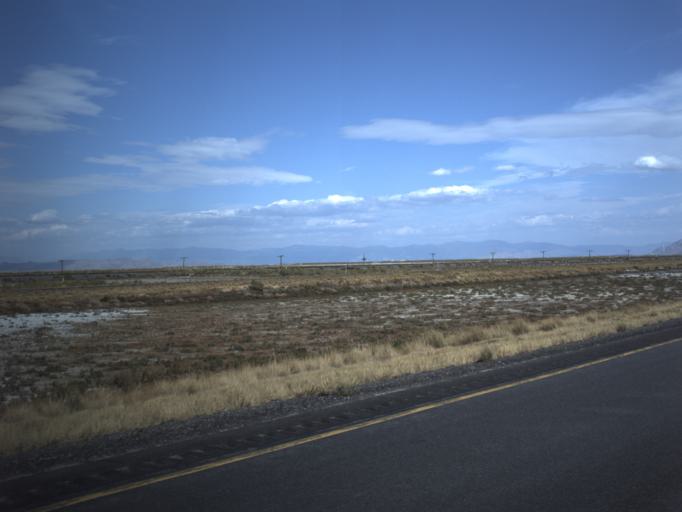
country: US
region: Utah
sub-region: Tooele County
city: Grantsville
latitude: 40.7023
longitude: -112.4985
